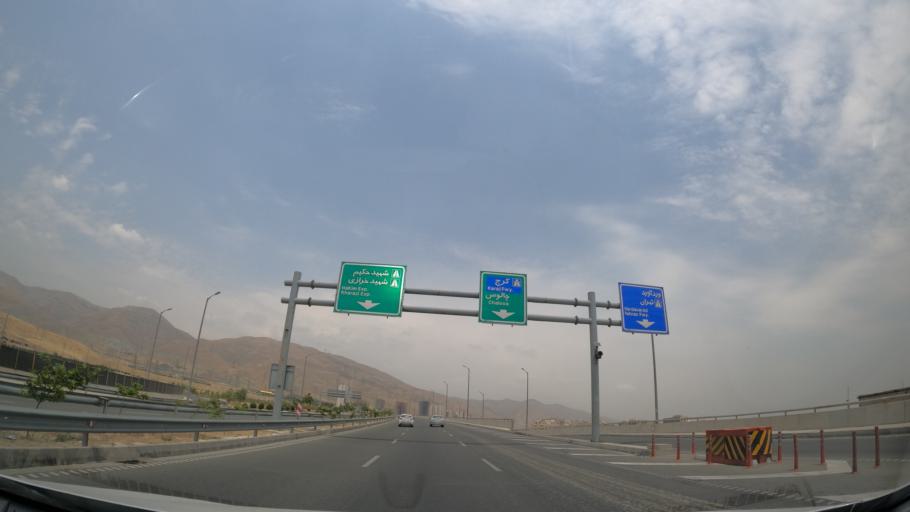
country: IR
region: Tehran
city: Shahr-e Qods
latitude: 35.7399
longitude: 51.1227
